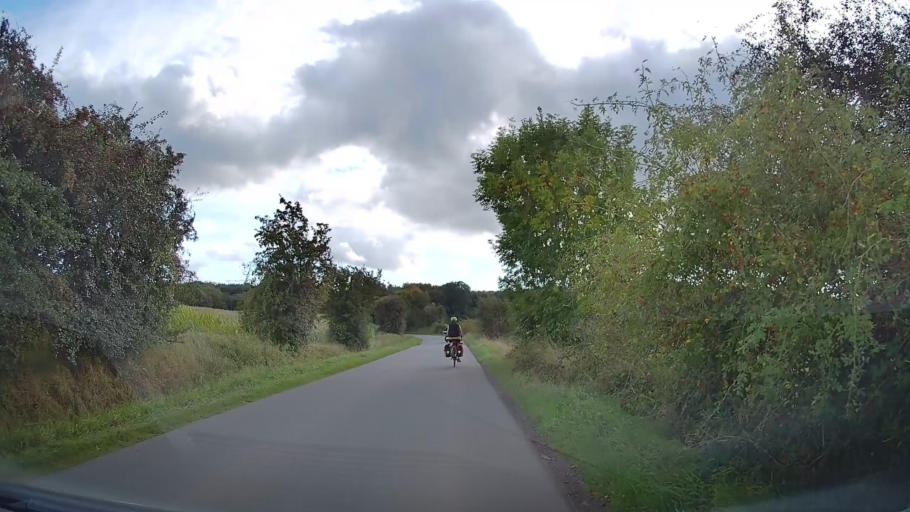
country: DE
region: Schleswig-Holstein
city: Steinberg
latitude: 54.7894
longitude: 9.7793
